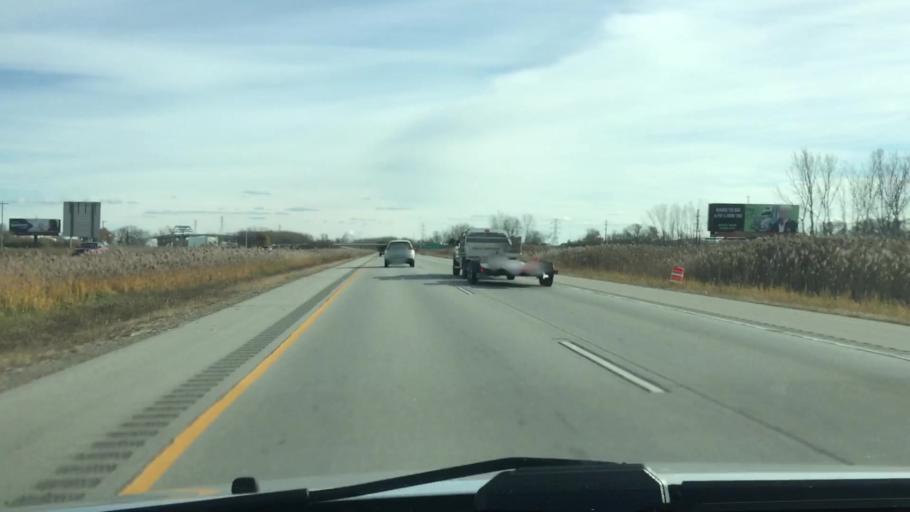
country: US
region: Wisconsin
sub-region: Brown County
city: Green Bay
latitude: 44.5457
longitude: -88.0335
